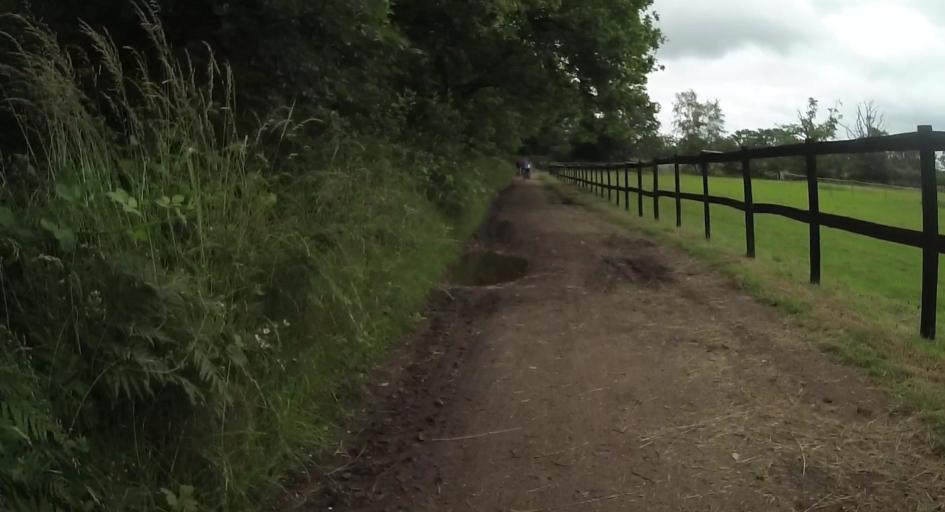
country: GB
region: England
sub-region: Hampshire
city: Eversley
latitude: 51.3566
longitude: -0.8763
